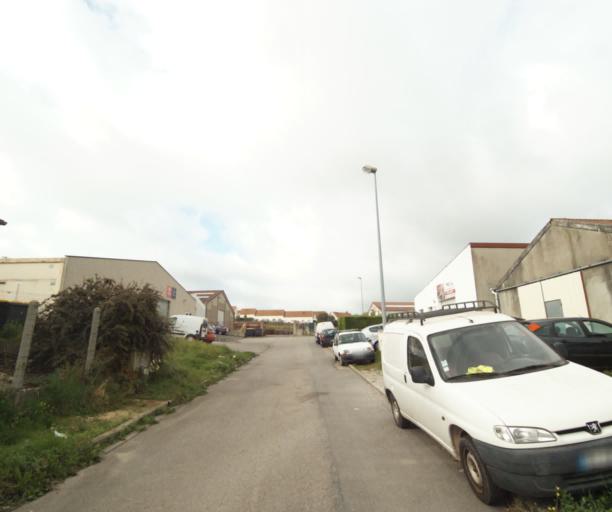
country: FR
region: Nord-Pas-de-Calais
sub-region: Departement du Pas-de-Calais
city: Etaples
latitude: 50.5201
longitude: 1.6580
